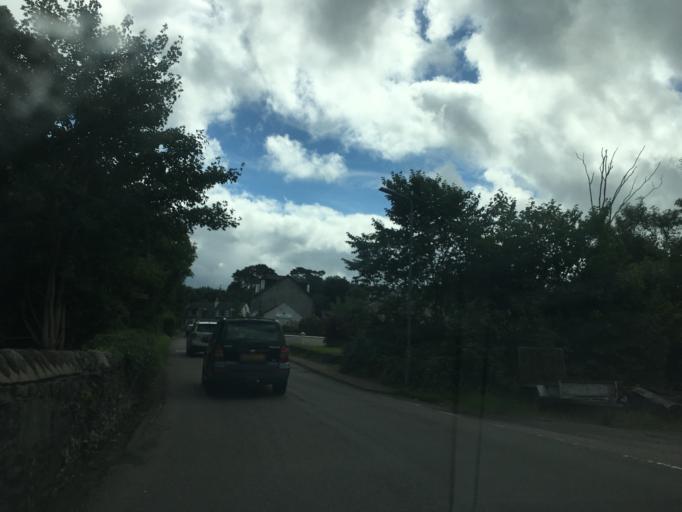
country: GB
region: Scotland
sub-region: Argyll and Bute
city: Tarbert
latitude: 55.8938
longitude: -5.2454
